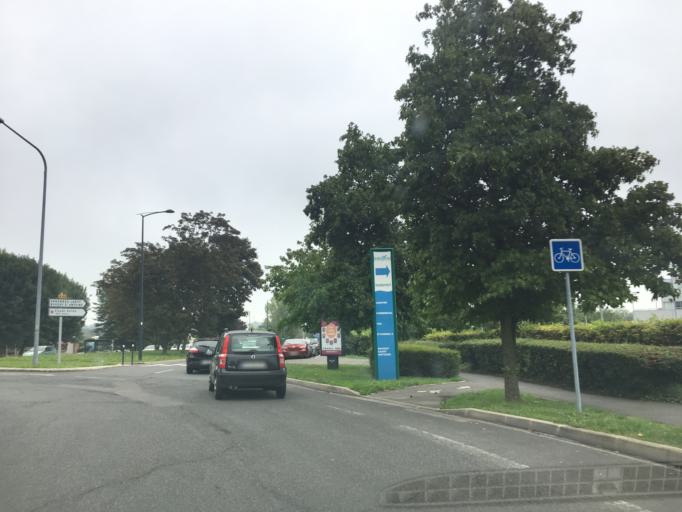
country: FR
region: Ile-de-France
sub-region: Departement de l'Essonne
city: Boussy-Saint-Antoine
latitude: 48.6830
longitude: 2.5328
